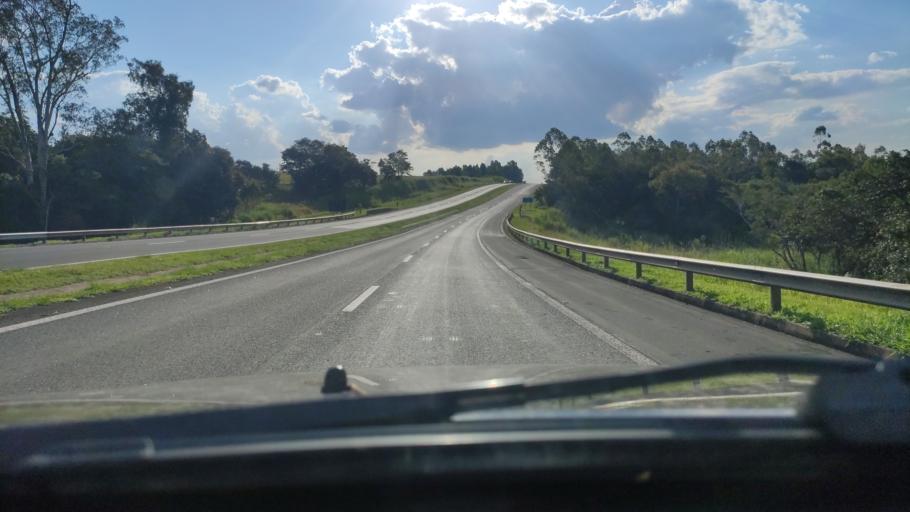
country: BR
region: Sao Paulo
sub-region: Itapira
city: Itapira
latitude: -22.4526
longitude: -46.8727
